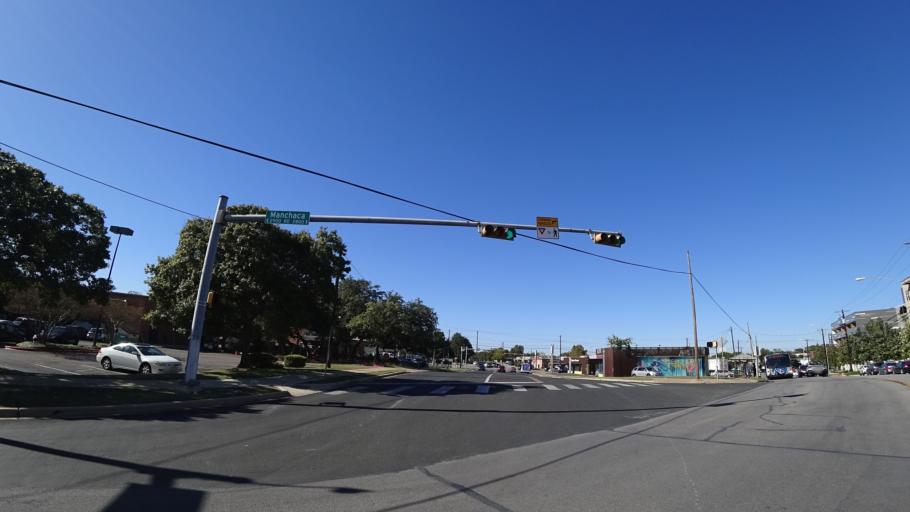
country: US
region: Texas
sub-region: Travis County
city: Rollingwood
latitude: 30.2426
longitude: -97.7817
